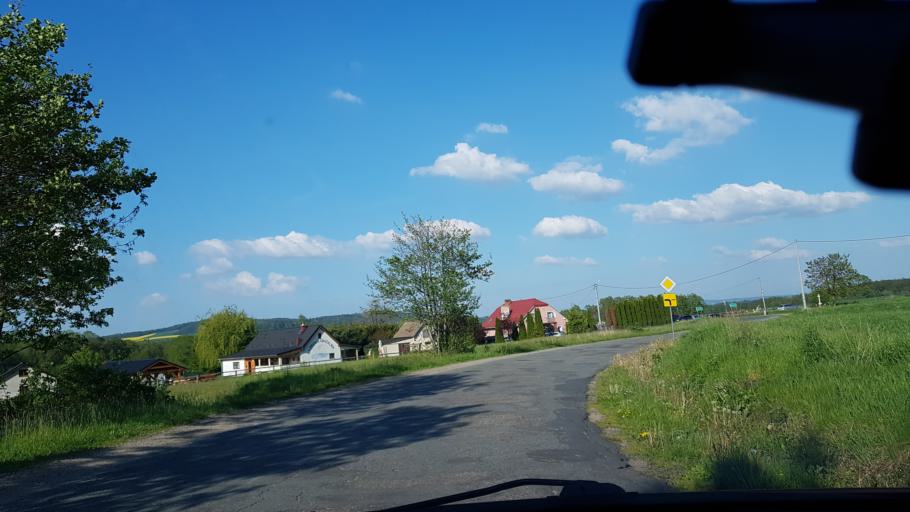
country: PL
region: Lower Silesian Voivodeship
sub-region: Powiat dzierzoniowski
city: Ostroszowice
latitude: 50.5993
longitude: 16.6586
